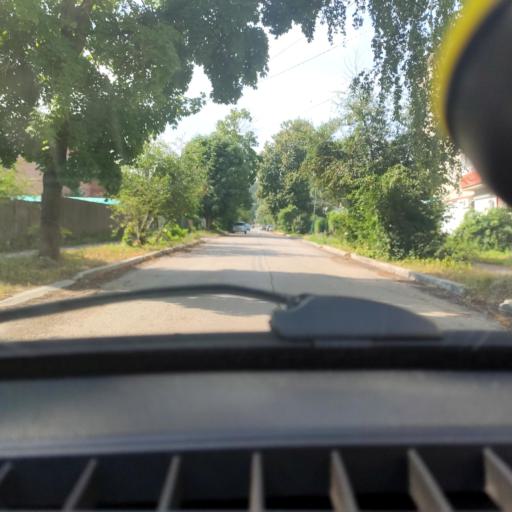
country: RU
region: Samara
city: Zhigulevsk
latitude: 53.4058
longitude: 49.4833
